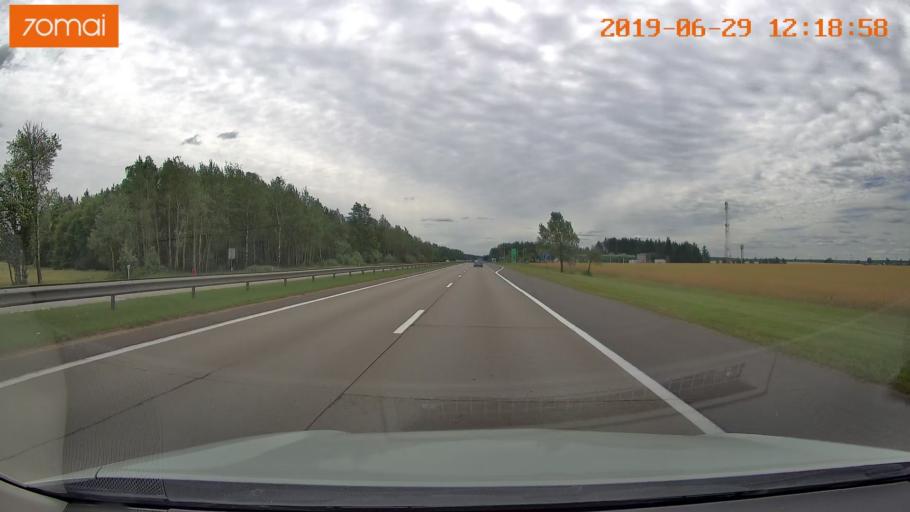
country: BY
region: Minsk
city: Samakhvalavichy
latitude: 53.5671
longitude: 27.4716
